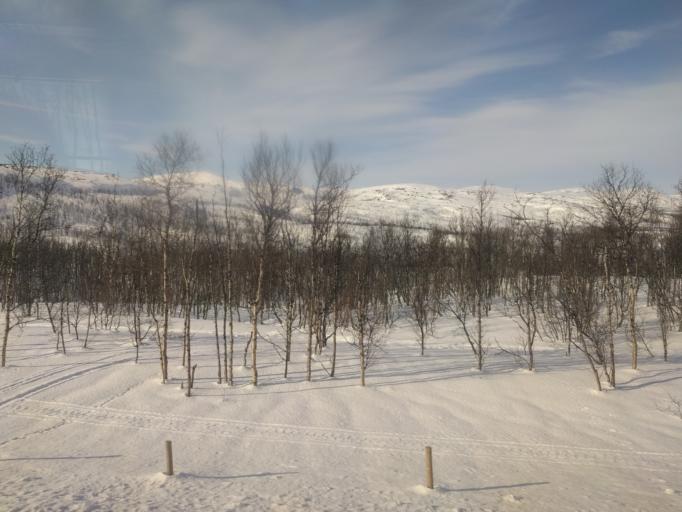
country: NO
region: Troms
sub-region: Bardu
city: Setermoen
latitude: 68.4255
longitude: 18.4472
